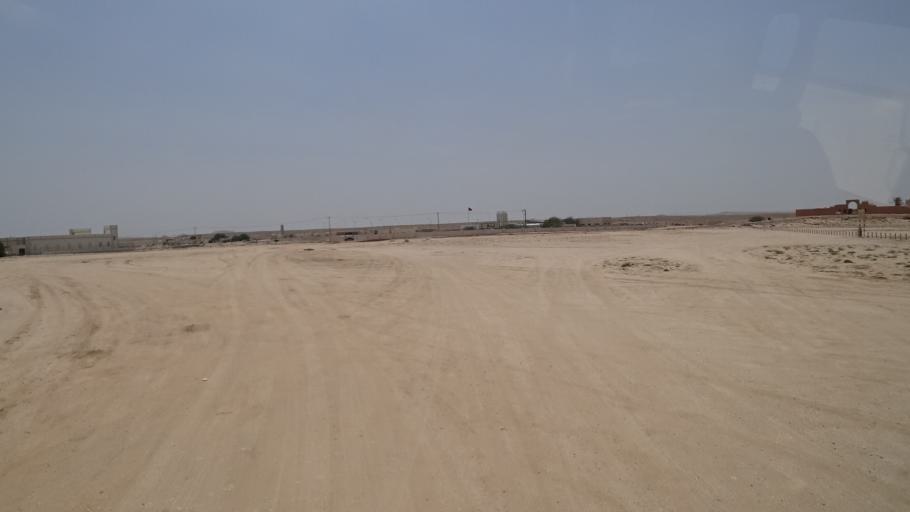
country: OM
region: Ash Sharqiyah
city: Sur
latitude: 22.5317
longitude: 59.7650
